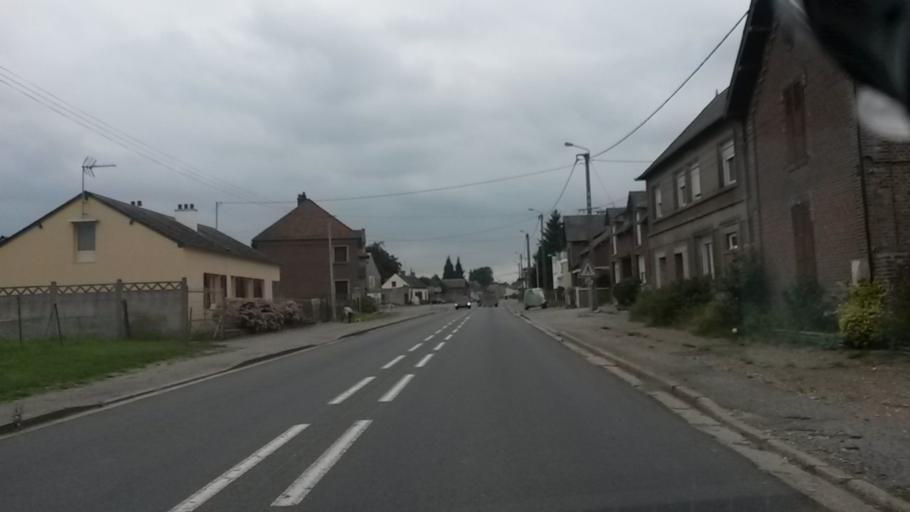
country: FR
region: Picardie
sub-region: Departement de la Somme
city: Hornoy-le-Bourg
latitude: 49.7744
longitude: 1.8615
